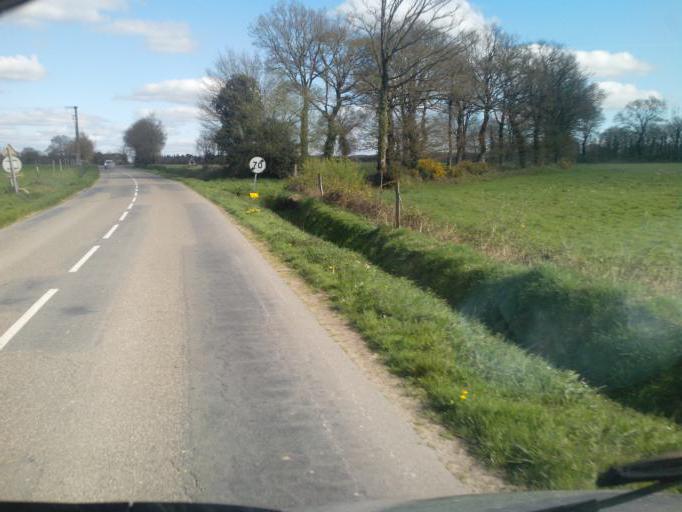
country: FR
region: Brittany
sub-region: Departement d'Ille-et-Vilaine
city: Plelan-le-Grand
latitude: 47.9912
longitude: -2.0674
